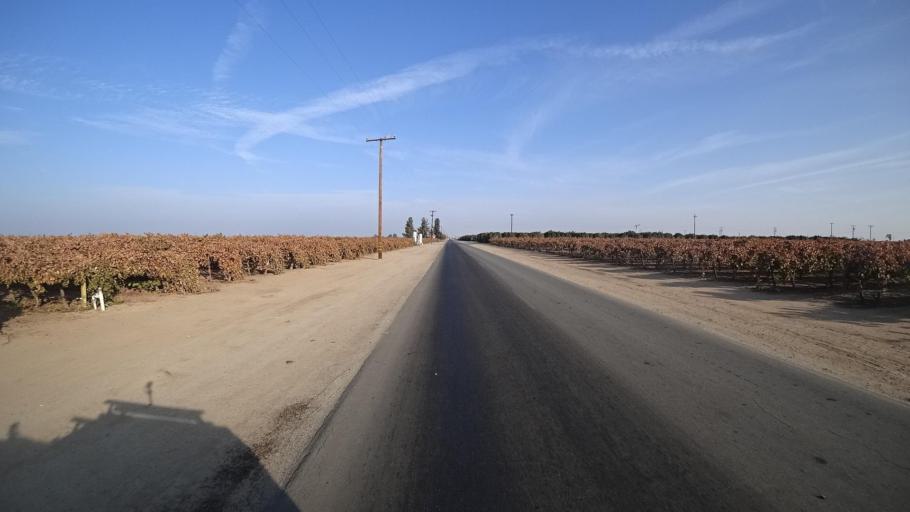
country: US
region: California
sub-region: Kern County
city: Delano
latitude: 35.7569
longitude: -119.1874
